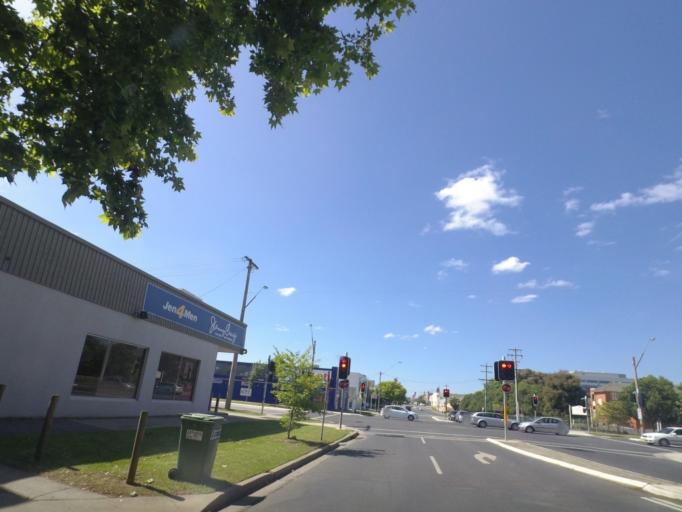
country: AU
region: New South Wales
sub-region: Albury Municipality
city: South Albury
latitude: -36.0851
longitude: 146.9148
